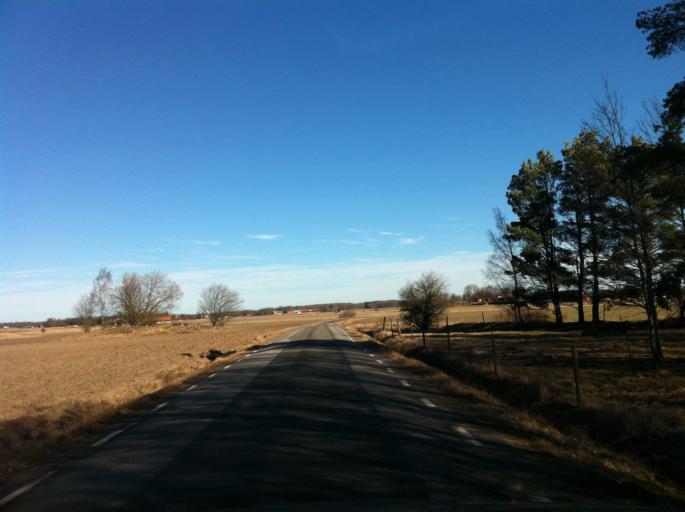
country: SE
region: Vaestra Goetaland
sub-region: Toreboda Kommun
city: Toereboda
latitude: 58.5841
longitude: 14.0890
